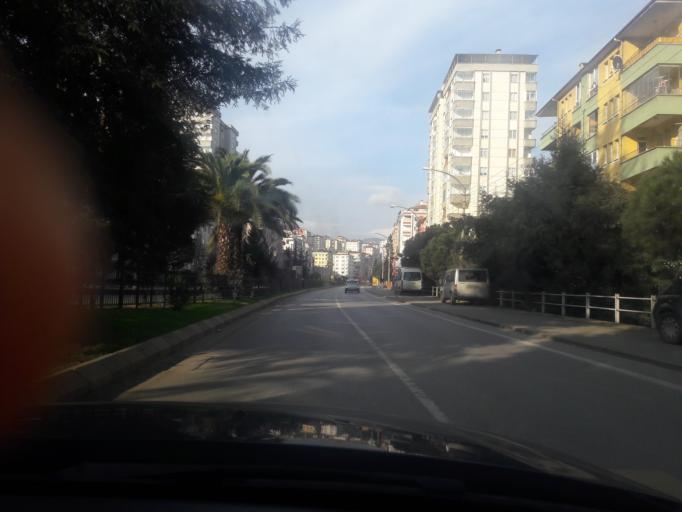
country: TR
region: Trabzon
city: Trabzon
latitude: 40.9984
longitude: 39.6919
